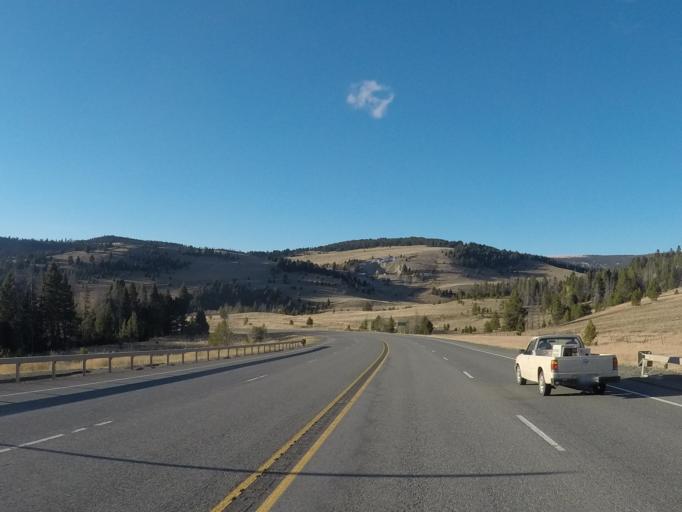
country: US
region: Montana
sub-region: Lewis and Clark County
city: Helena West Side
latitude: 46.5599
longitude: -112.3719
